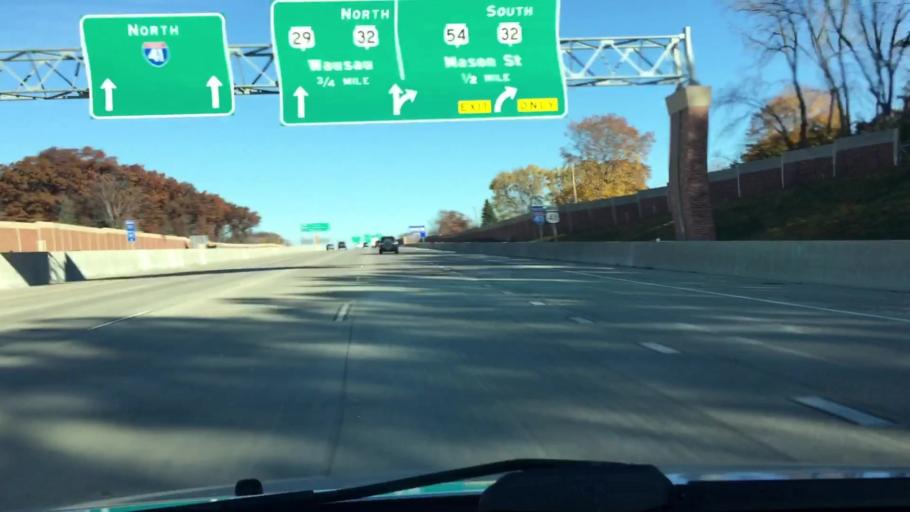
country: US
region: Wisconsin
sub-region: Brown County
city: Howard
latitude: 44.5149
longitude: -88.0823
